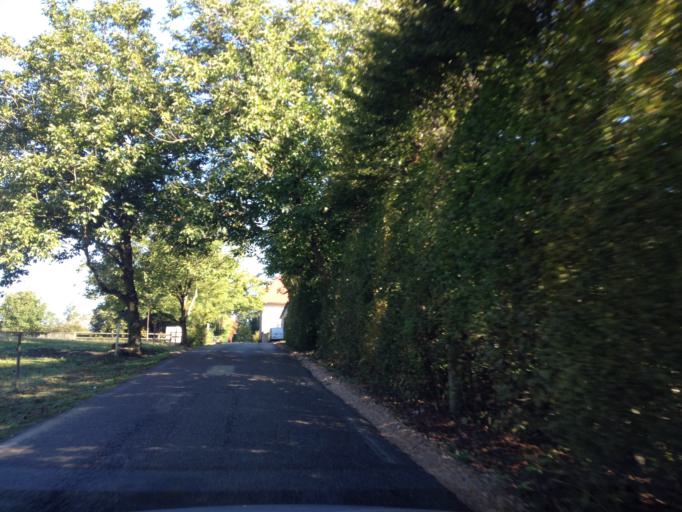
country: FR
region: Rhone-Alpes
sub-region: Departement de l'Isere
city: Morestel
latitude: 45.6692
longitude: 5.4566
